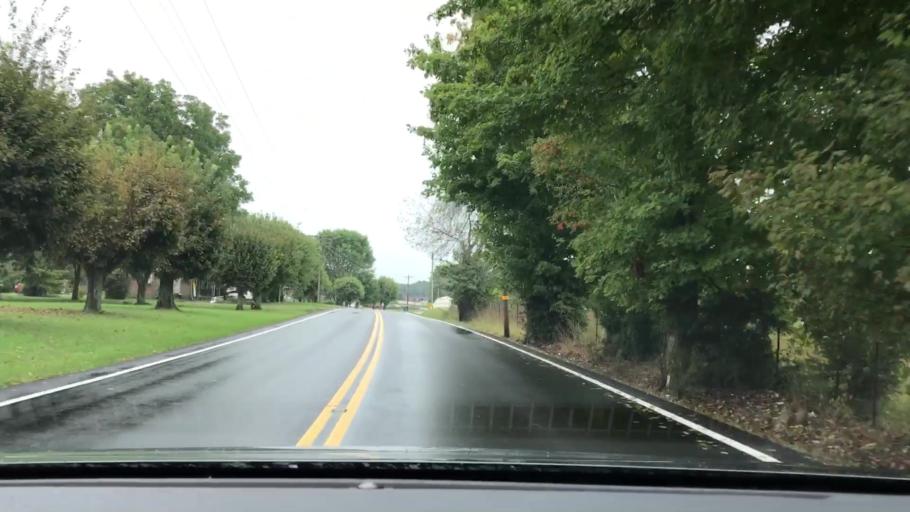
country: US
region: Tennessee
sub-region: Macon County
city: Red Boiling Springs
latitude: 36.5001
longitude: -85.8670
